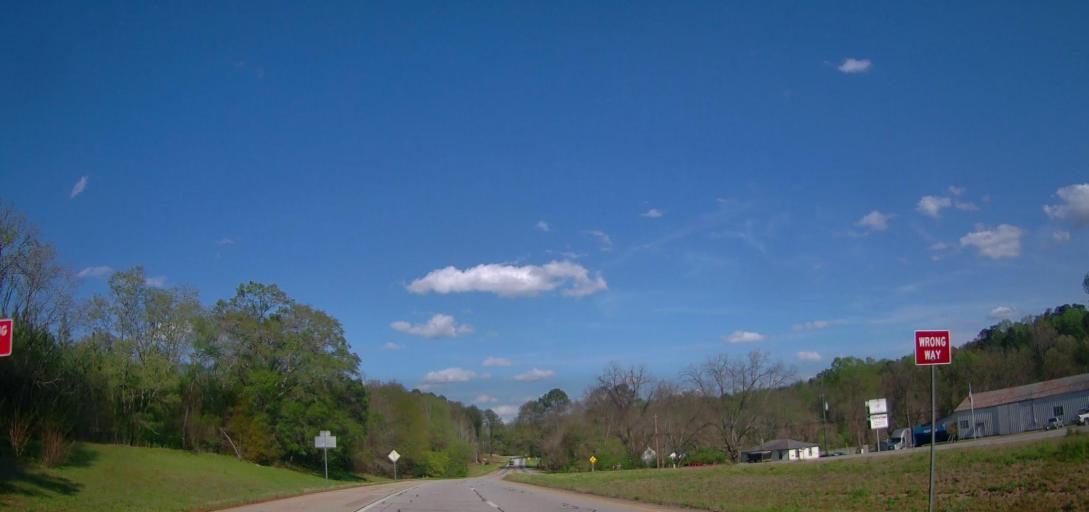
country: US
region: Georgia
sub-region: Baldwin County
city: Hardwick
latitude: 33.0858
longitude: -83.2065
